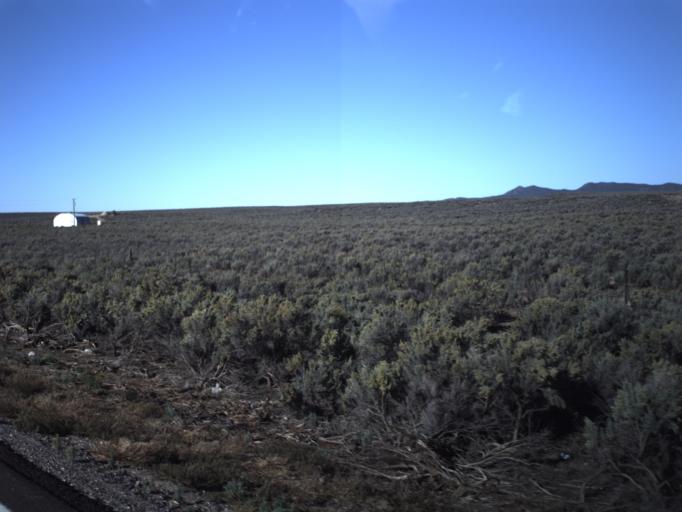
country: US
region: Utah
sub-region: Washington County
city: Enterprise
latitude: 37.7670
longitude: -113.9814
